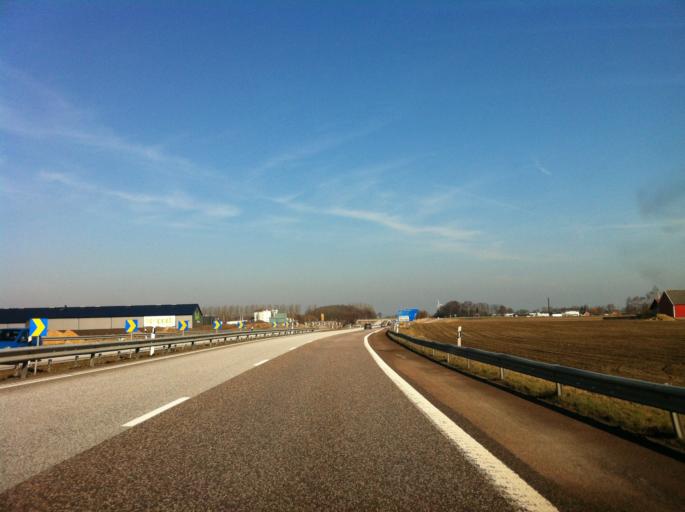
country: SE
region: Skane
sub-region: Angelholms Kommun
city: Strovelstorp
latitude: 56.1877
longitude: 12.8527
